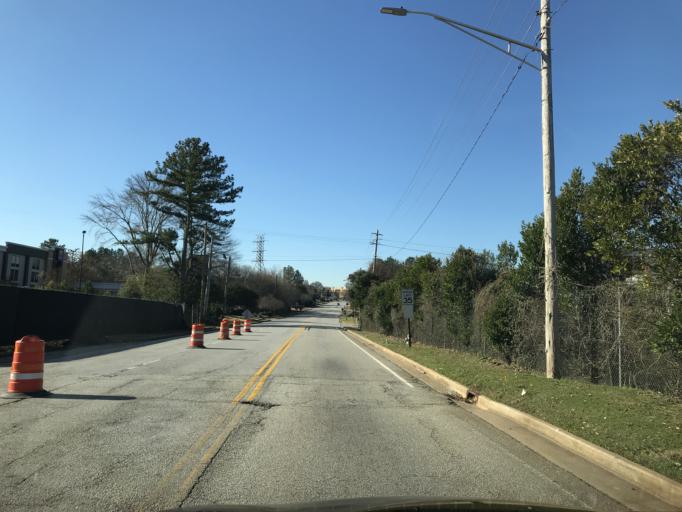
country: US
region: Georgia
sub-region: Fulton County
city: College Park
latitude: 33.6274
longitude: -84.4505
